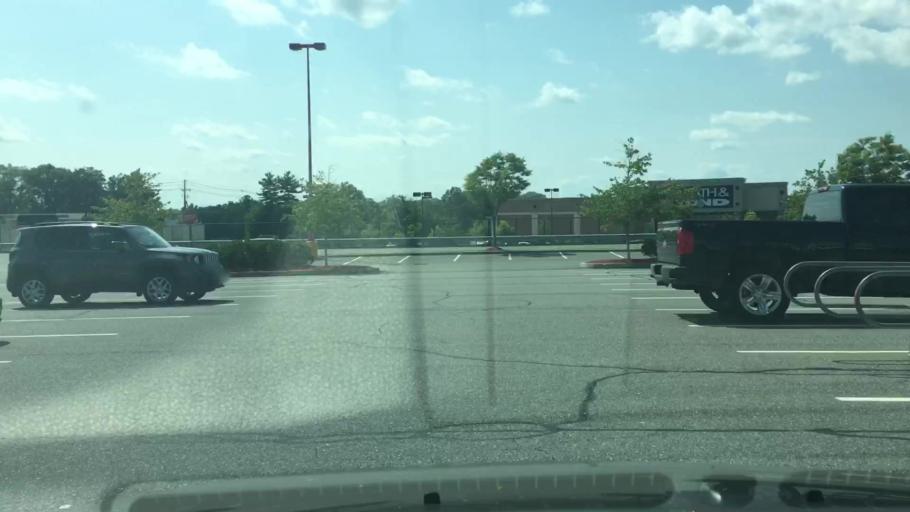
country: US
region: Massachusetts
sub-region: Worcester County
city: Milford
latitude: 42.1606
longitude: -71.4996
